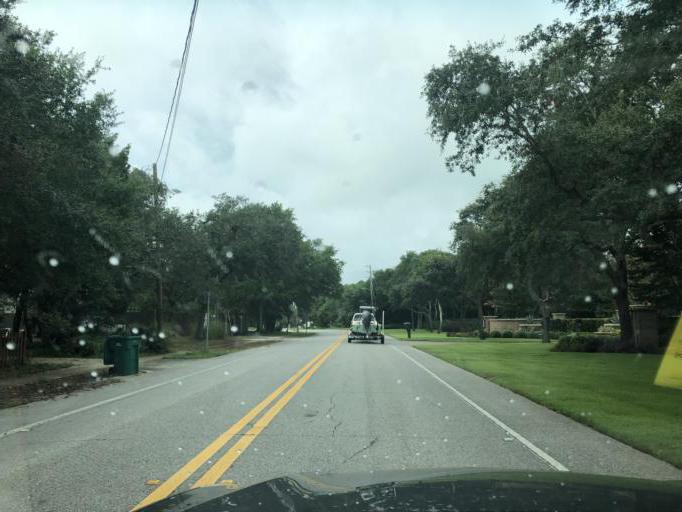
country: US
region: Florida
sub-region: Okaloosa County
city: Destin
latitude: 30.4020
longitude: -86.5081
